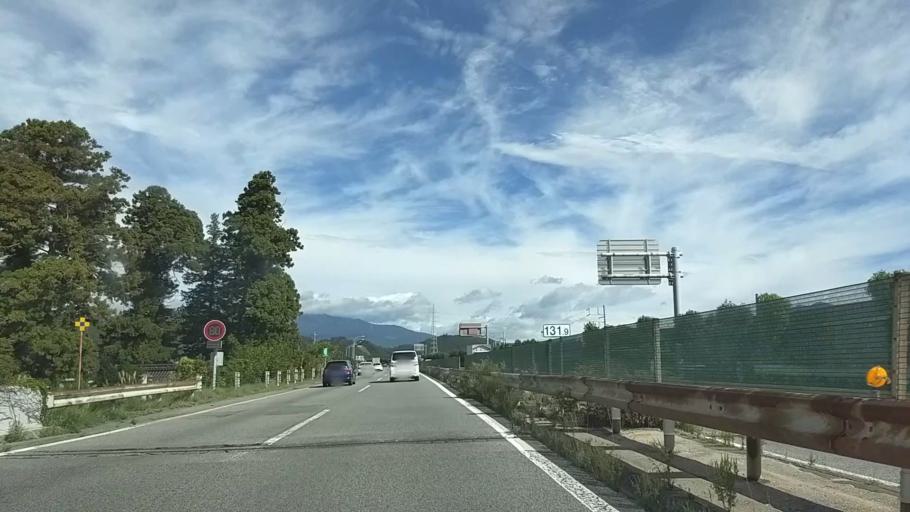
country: JP
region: Yamanashi
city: Nirasaki
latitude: 35.7768
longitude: 138.4226
